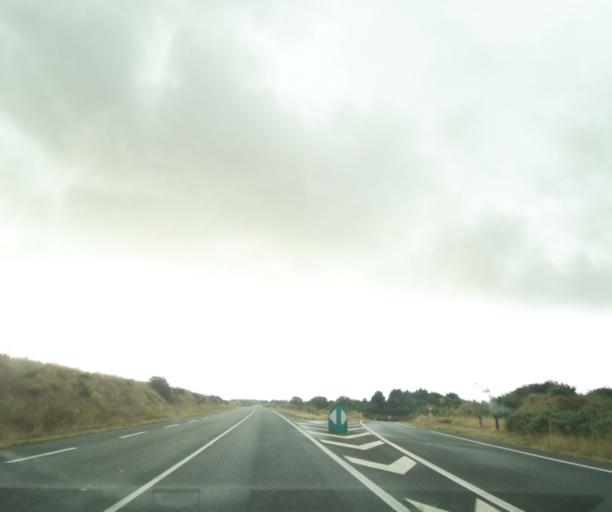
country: FR
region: Pays de la Loire
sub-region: Departement de la Vendee
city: Saint-Hilaire-de-Talmont
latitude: 46.4643
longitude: -1.6408
